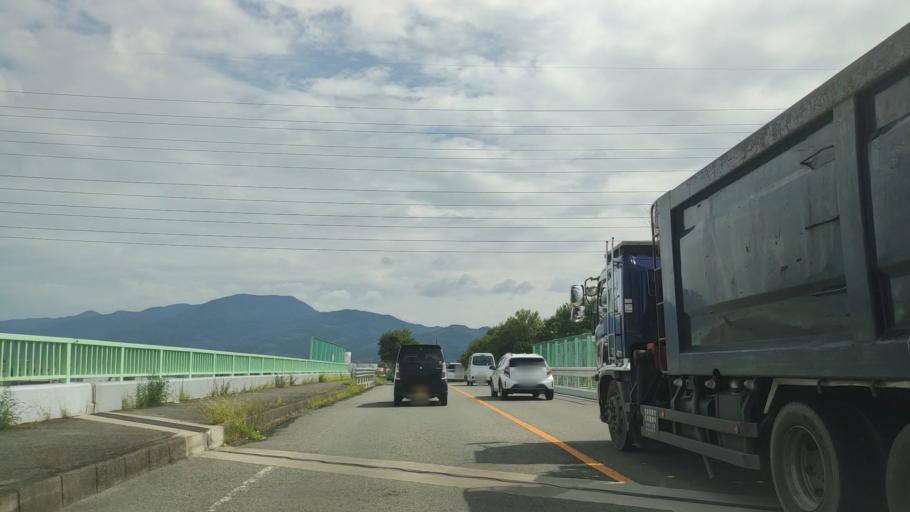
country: JP
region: Wakayama
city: Iwade
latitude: 34.2621
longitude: 135.3370
